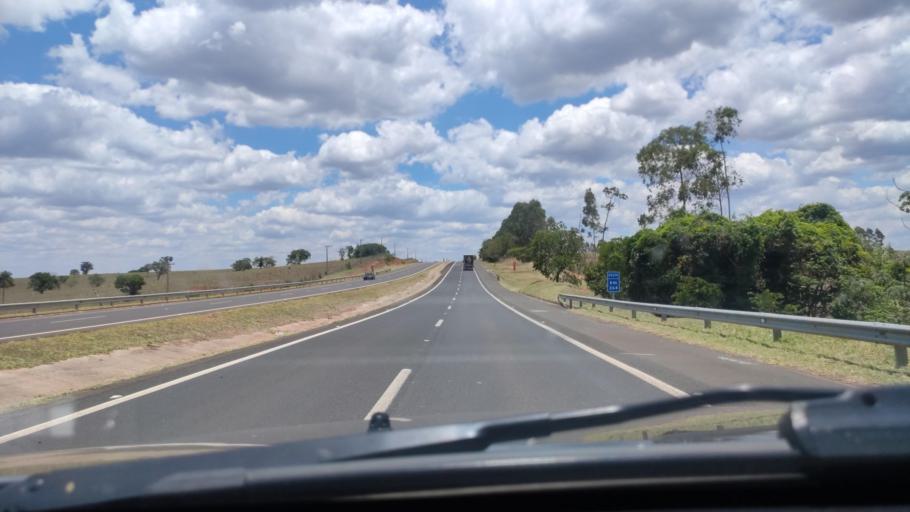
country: BR
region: Sao Paulo
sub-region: Duartina
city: Duartina
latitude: -22.4991
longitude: -49.2717
